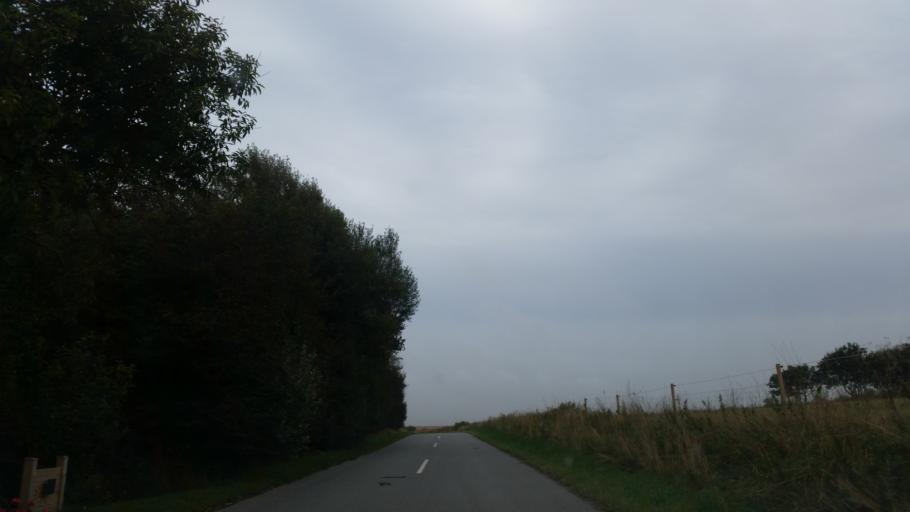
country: DK
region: South Denmark
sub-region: Tonder Kommune
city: Sherrebek
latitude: 55.0903
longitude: 8.6772
